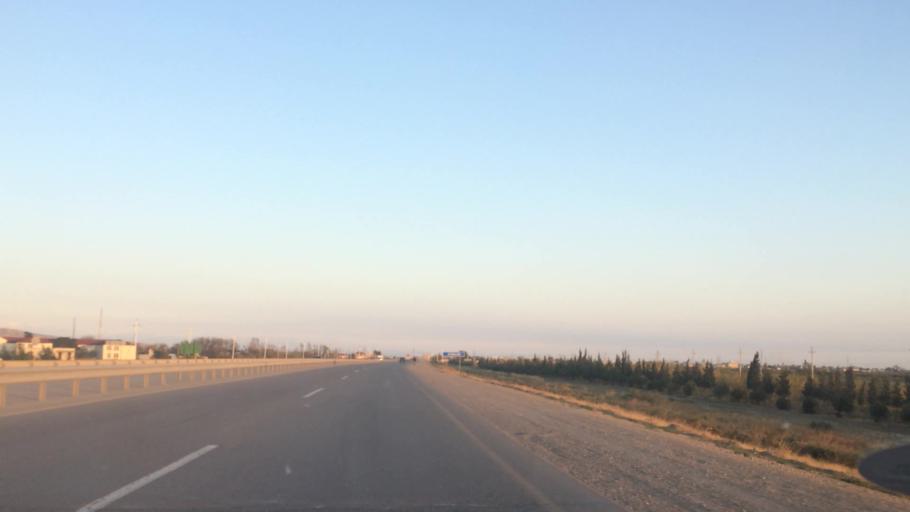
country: AZ
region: Baki
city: Qobustan
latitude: 39.9765
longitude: 49.2475
